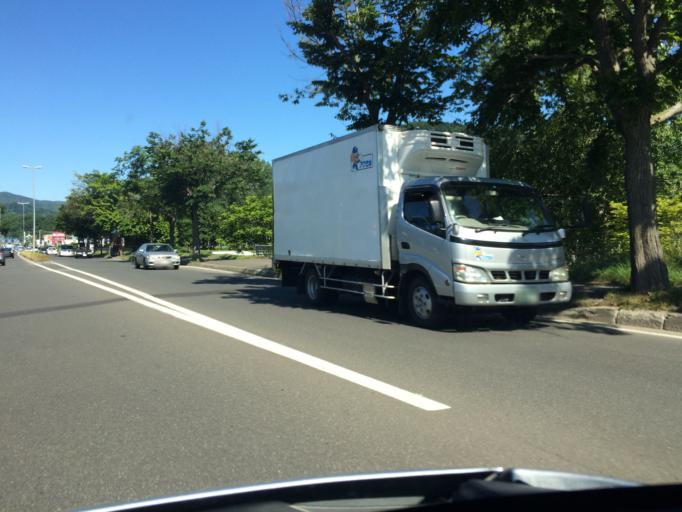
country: JP
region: Hokkaido
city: Sapporo
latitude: 42.9989
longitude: 141.3437
